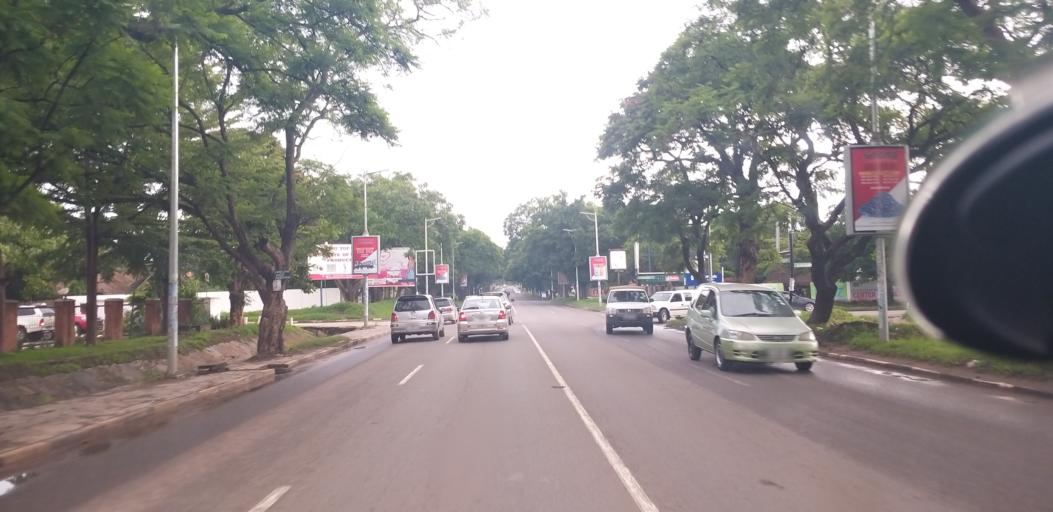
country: ZM
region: Lusaka
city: Lusaka
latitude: -15.4150
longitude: 28.2905
